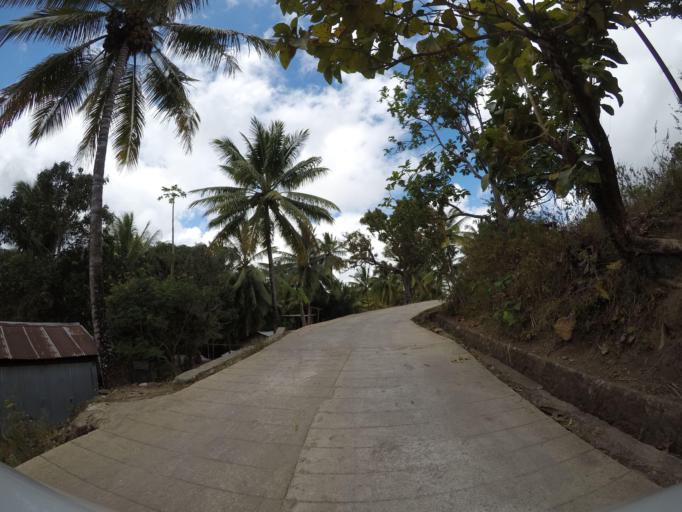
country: TL
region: Lautem
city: Lospalos
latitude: -8.5483
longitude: 126.8310
